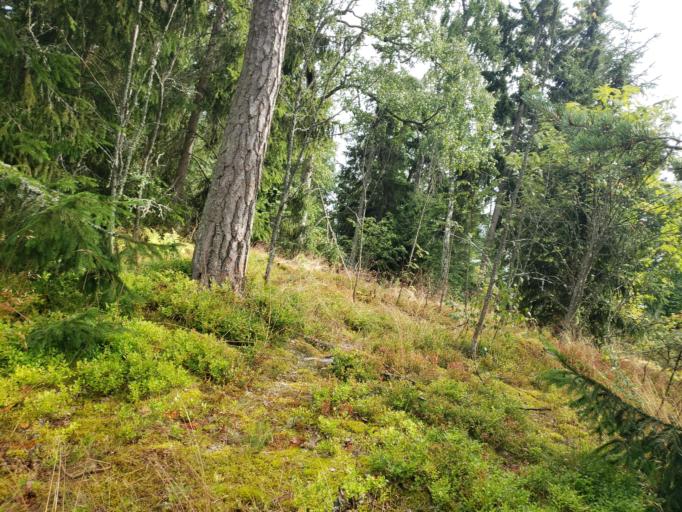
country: FI
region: Uusimaa
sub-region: Helsinki
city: Koukkuniemi
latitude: 60.0948
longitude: 24.7515
